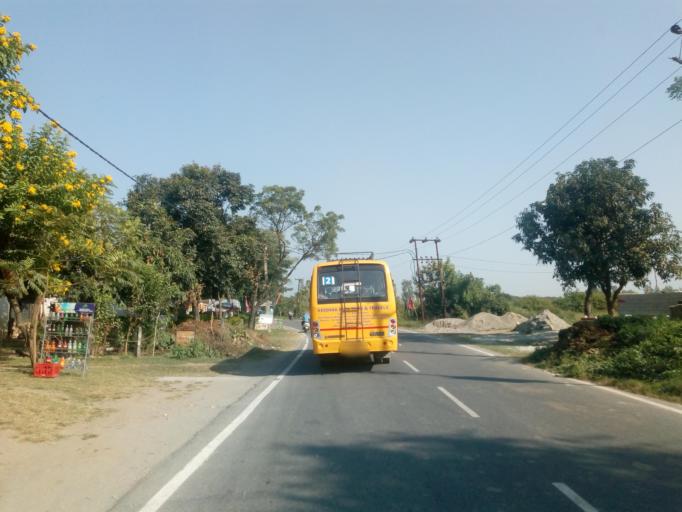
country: IN
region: Uttarakhand
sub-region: Dehradun
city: Harbatpur
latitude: 30.4413
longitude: 77.6907
